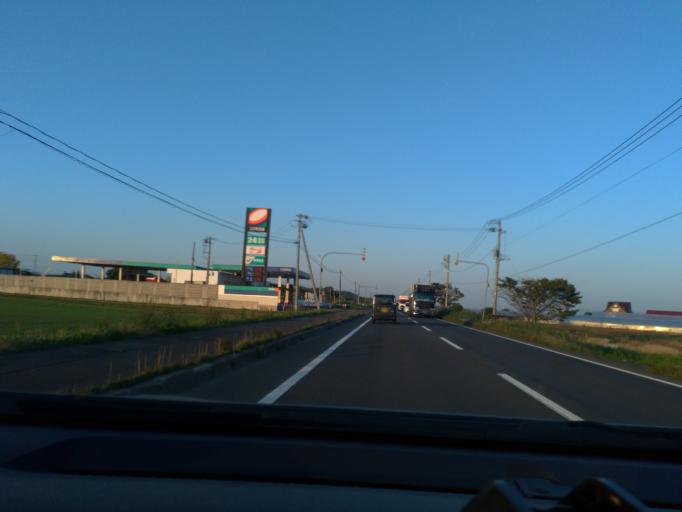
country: JP
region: Hokkaido
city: Tobetsu
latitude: 43.2171
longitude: 141.5323
